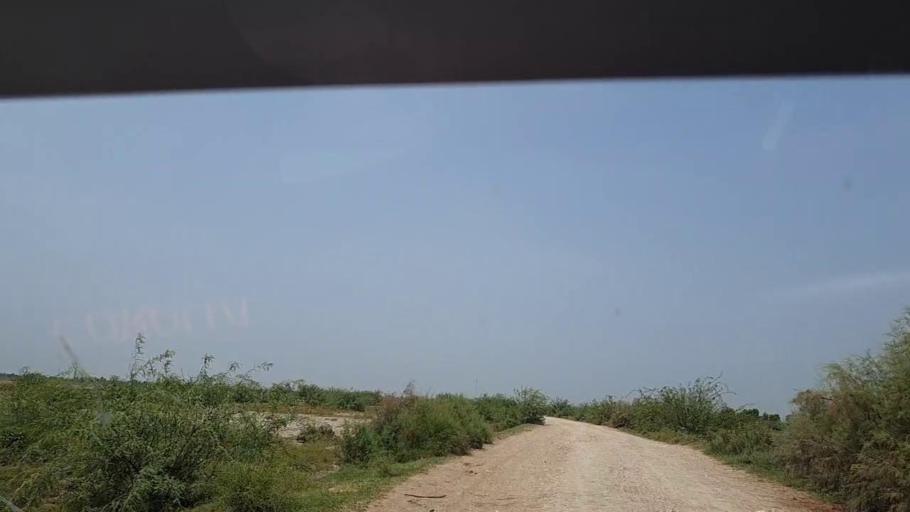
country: PK
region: Sindh
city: Adilpur
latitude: 27.9062
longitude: 69.2226
